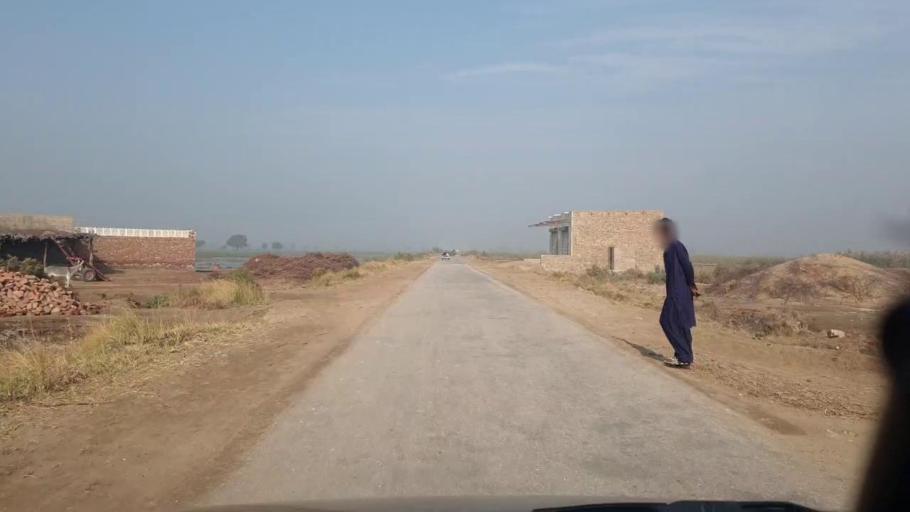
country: PK
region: Sindh
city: Shahdadpur
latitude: 25.9494
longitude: 68.5946
